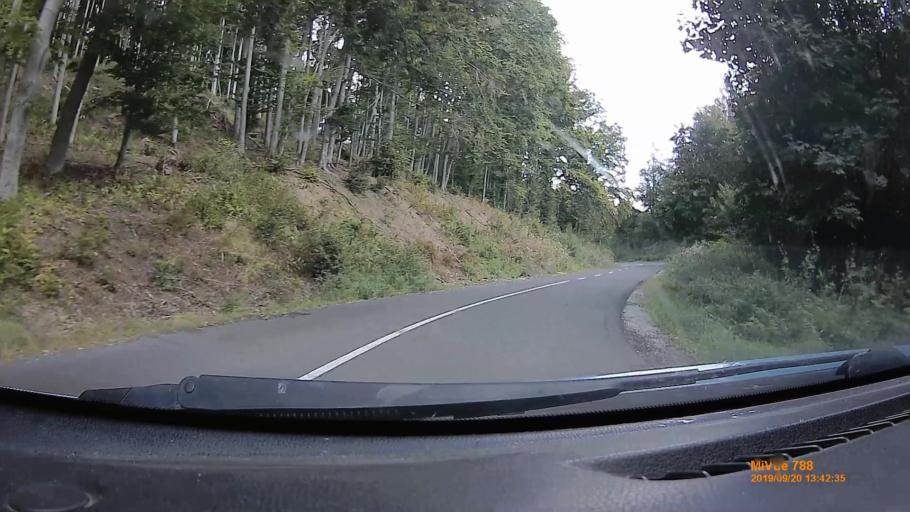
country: HU
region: Heves
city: Szilvasvarad
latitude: 48.0588
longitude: 20.5461
